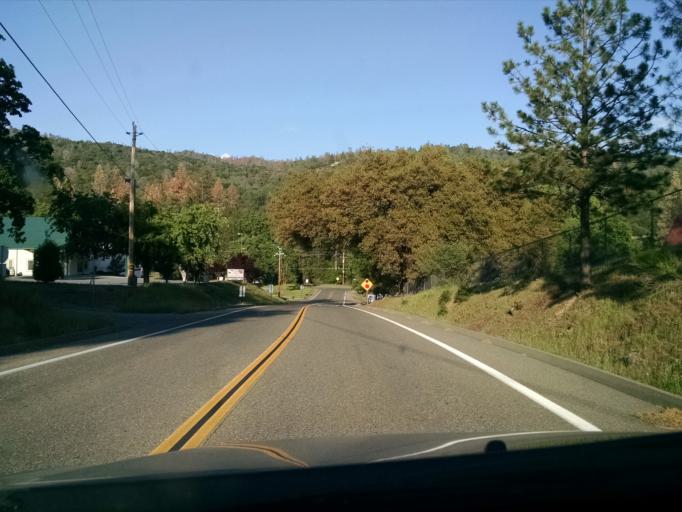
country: US
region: California
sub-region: Madera County
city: Oakhurst
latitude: 37.3297
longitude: -119.6290
